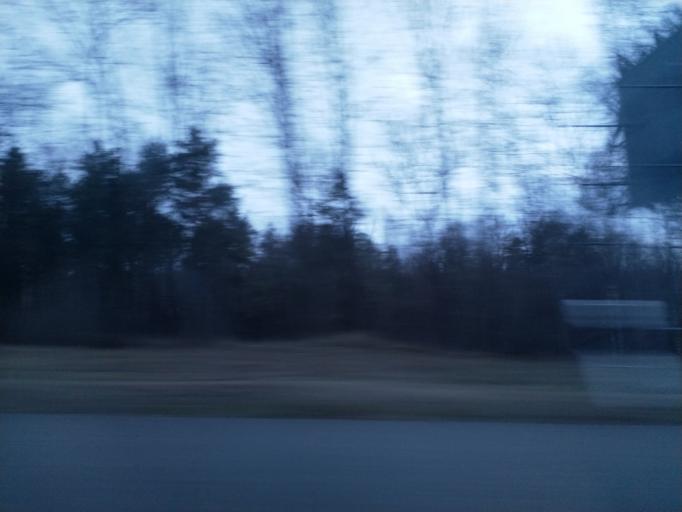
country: FR
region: Alsace
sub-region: Departement du Haut-Rhin
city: Kembs
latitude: 47.6720
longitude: 7.5236
